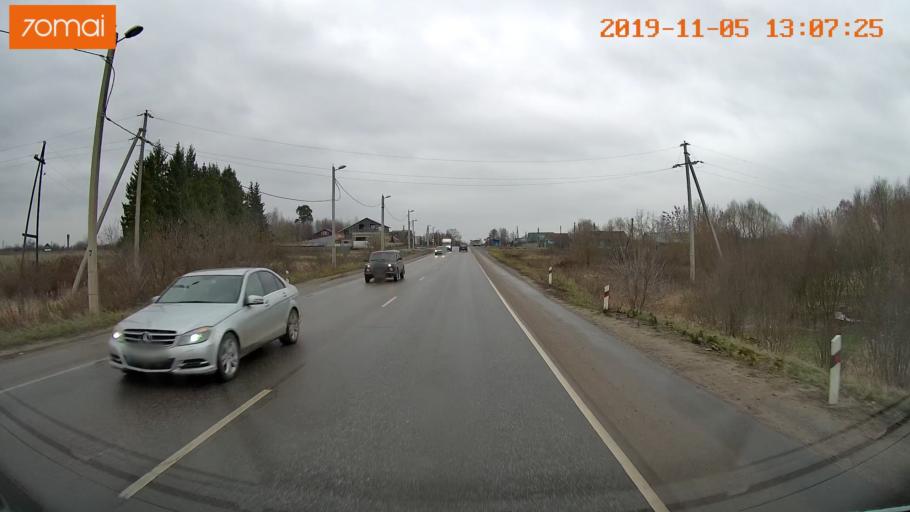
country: RU
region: Ivanovo
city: Kitovo
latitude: 56.8679
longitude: 41.2802
